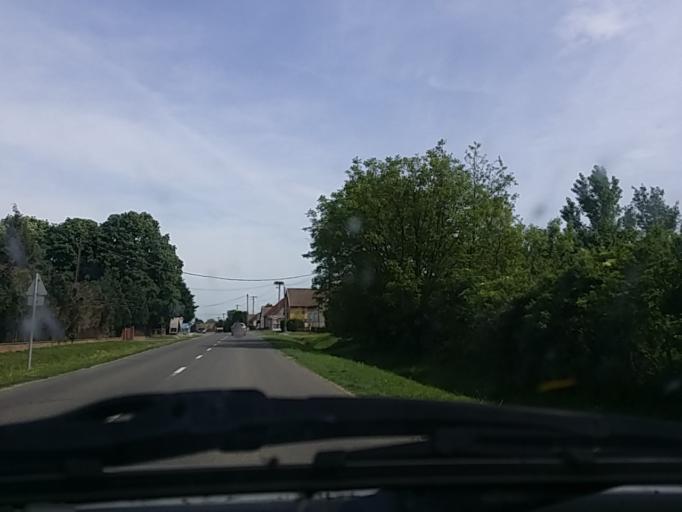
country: HU
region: Baranya
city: Harkany
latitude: 45.8350
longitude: 18.1790
